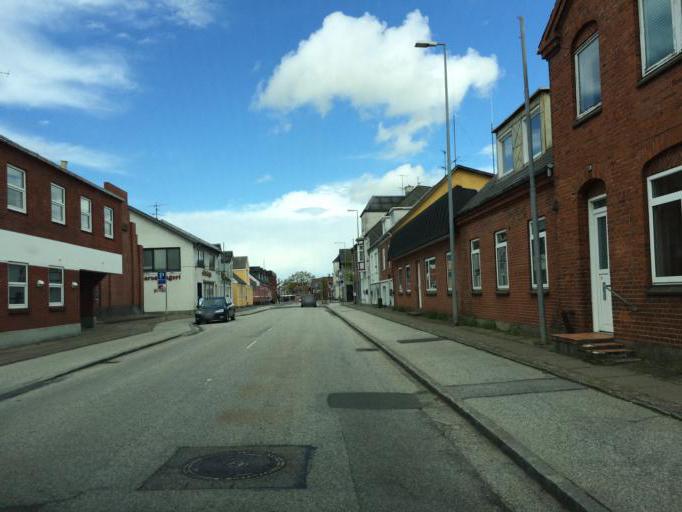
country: DK
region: North Denmark
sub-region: Vesthimmerland Kommune
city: Farso
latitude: 56.7700
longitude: 9.3403
